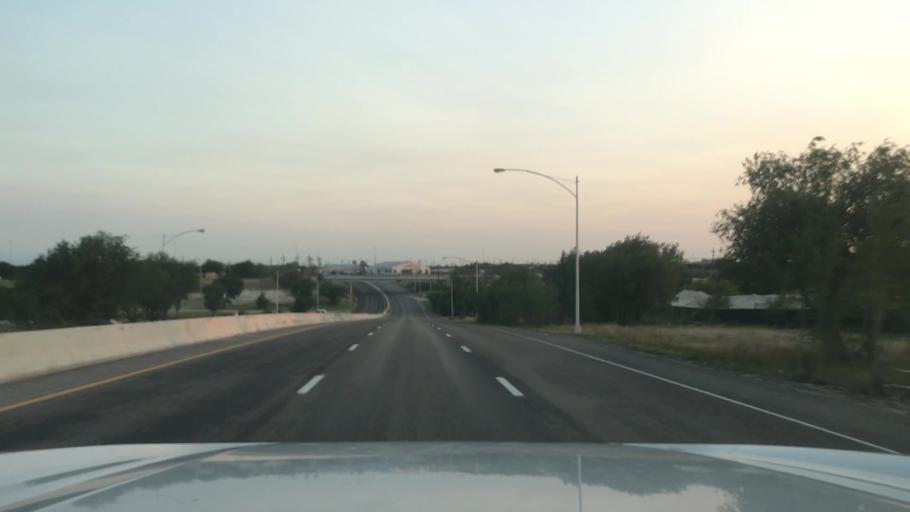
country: US
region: Texas
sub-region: Lubbock County
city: Lubbock
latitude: 33.6056
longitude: -101.8515
